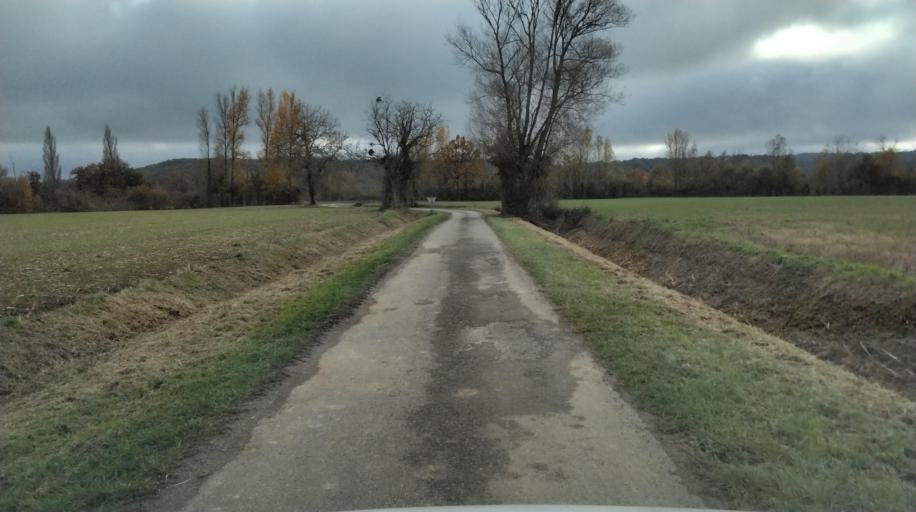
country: FR
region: Midi-Pyrenees
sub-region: Departement de la Haute-Garonne
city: Le Fousseret
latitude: 43.2727
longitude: 1.0640
